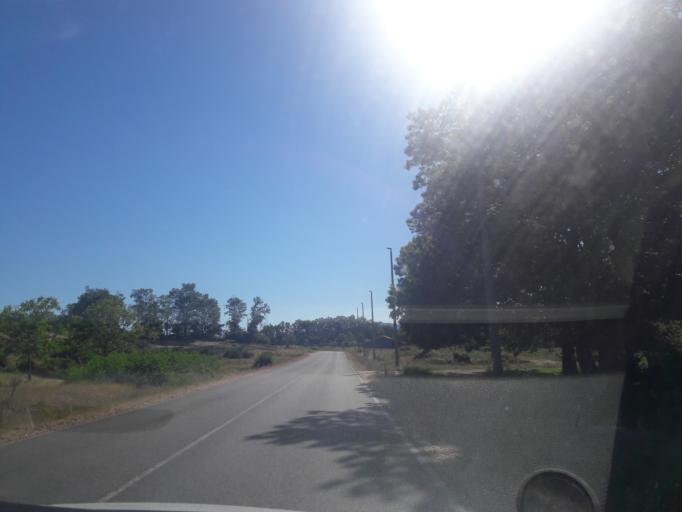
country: ES
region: Castille and Leon
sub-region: Provincia de Salamanca
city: Lagunilla
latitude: 40.3258
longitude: -5.9623
